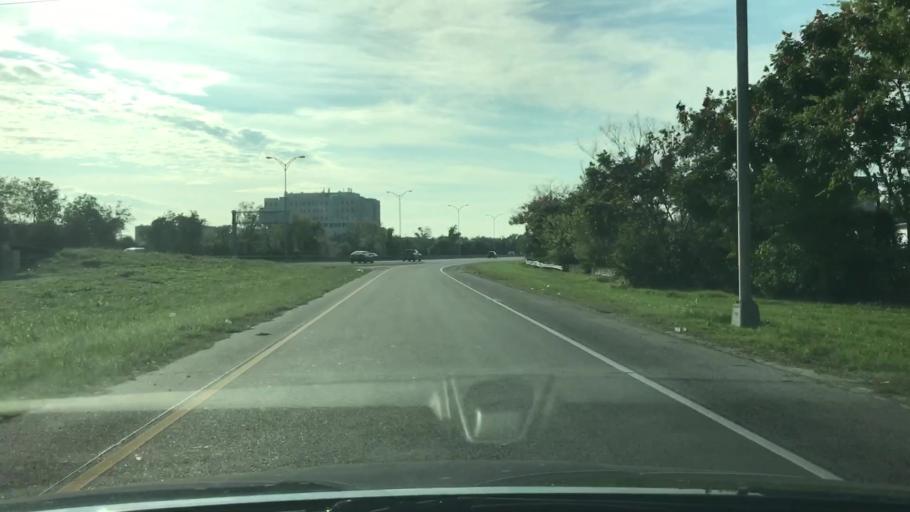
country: US
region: Louisiana
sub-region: Orleans Parish
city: New Orleans
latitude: 29.9933
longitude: -90.0790
